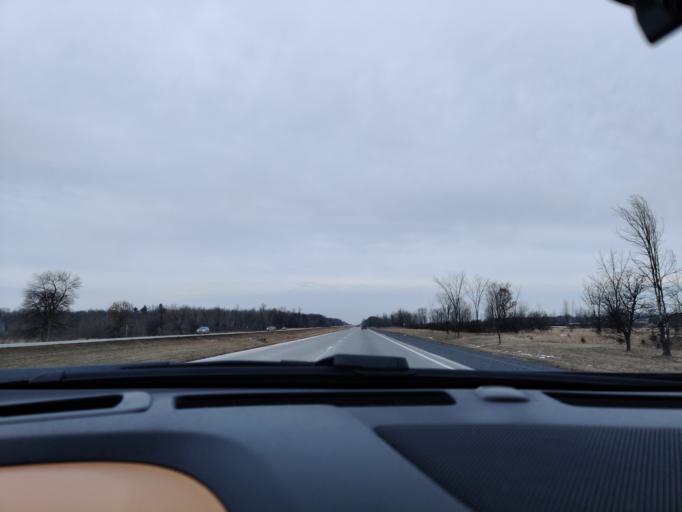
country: US
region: New York
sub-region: St. Lawrence County
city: Massena
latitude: 45.0310
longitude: -74.9483
